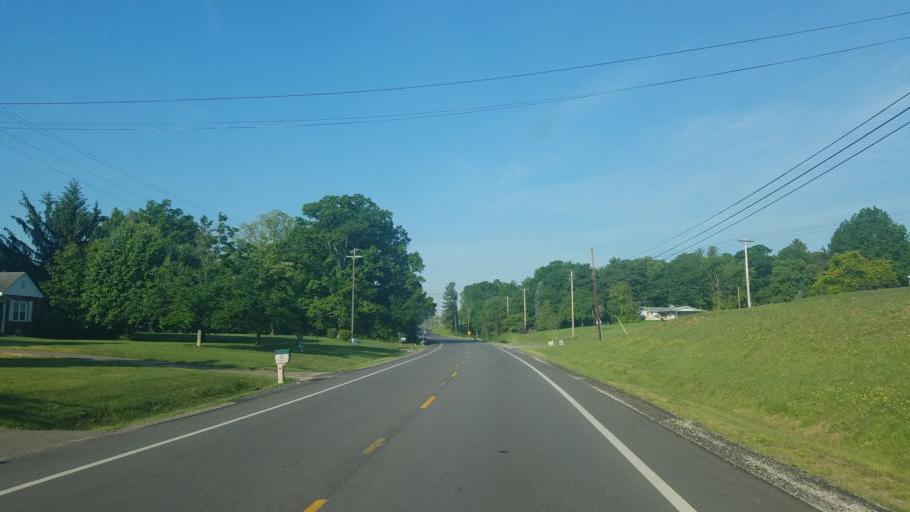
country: US
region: West Virginia
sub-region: Mason County
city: New Haven
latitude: 39.0655
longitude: -81.9448
